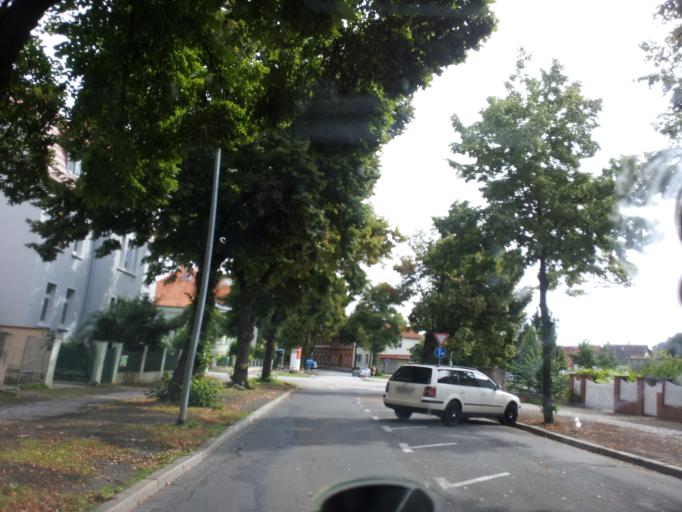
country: DE
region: Saxony-Anhalt
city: Quedlinburg
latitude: 51.7941
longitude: 11.1429
